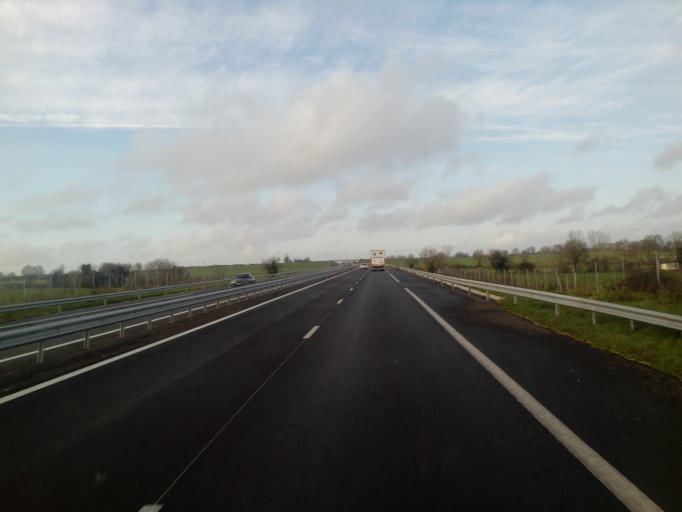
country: FR
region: Poitou-Charentes
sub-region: Departement des Deux-Sevres
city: Nueil-les-Aubiers
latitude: 46.8624
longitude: -0.5696
